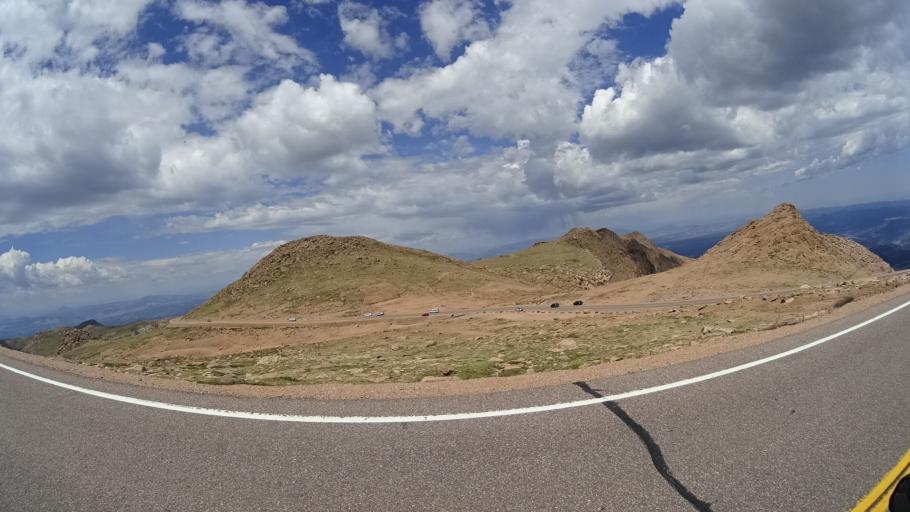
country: US
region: Colorado
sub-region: El Paso County
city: Cascade-Chipita Park
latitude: 38.8474
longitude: -105.0537
